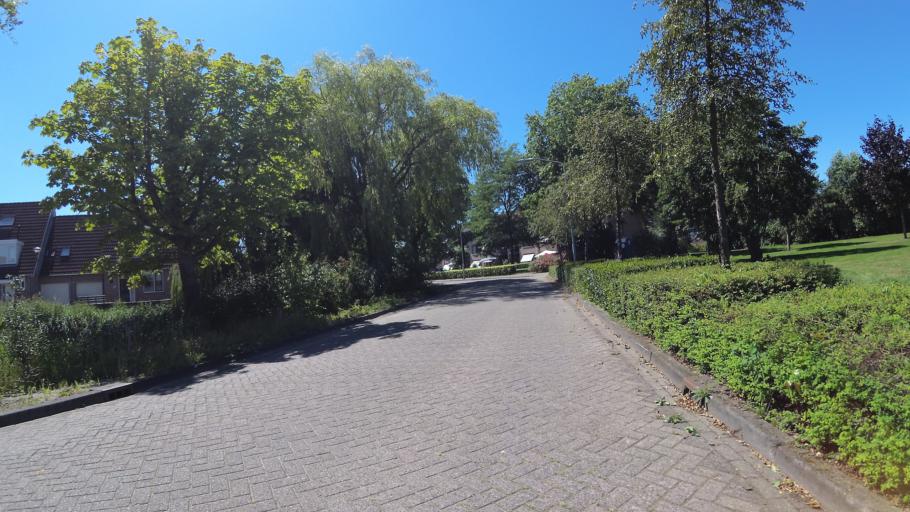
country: NL
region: North Brabant
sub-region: Gemeente Waalwijk
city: Waalwijk
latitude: 51.6754
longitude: 5.0167
